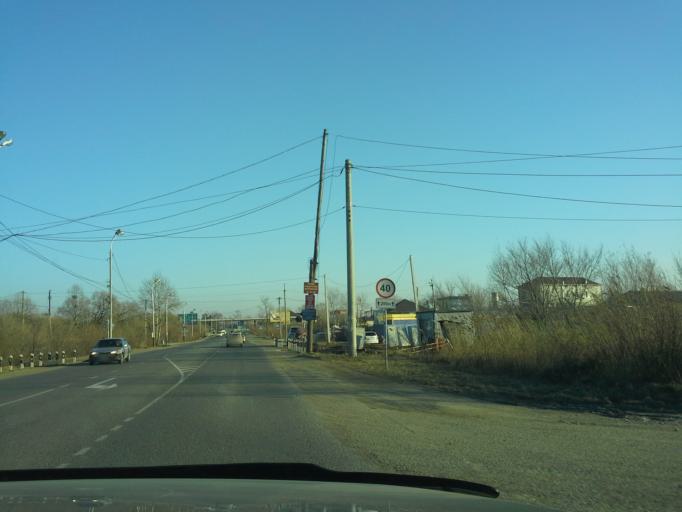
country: RU
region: Khabarovsk Krai
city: Topolevo
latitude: 48.4747
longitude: 135.1701
